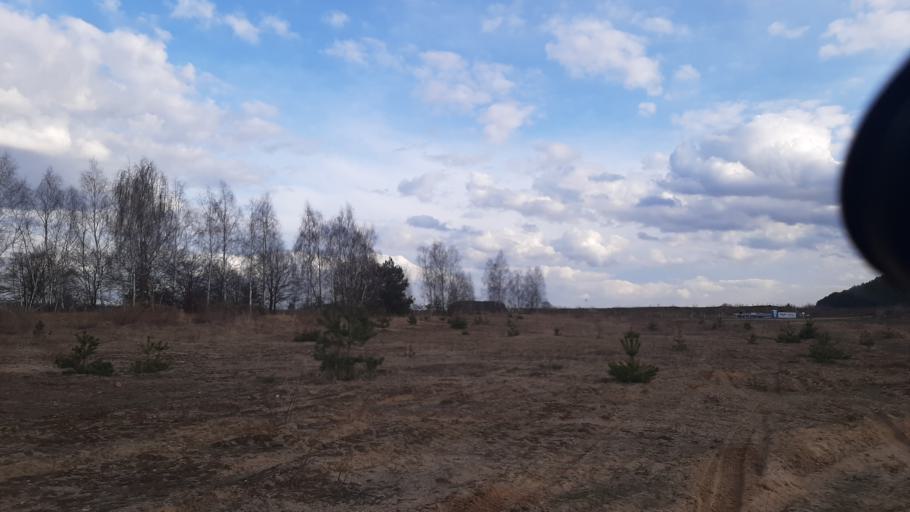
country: PL
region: Lublin Voivodeship
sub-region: Powiat lubelski
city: Jastkow
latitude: 51.3810
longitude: 22.4357
